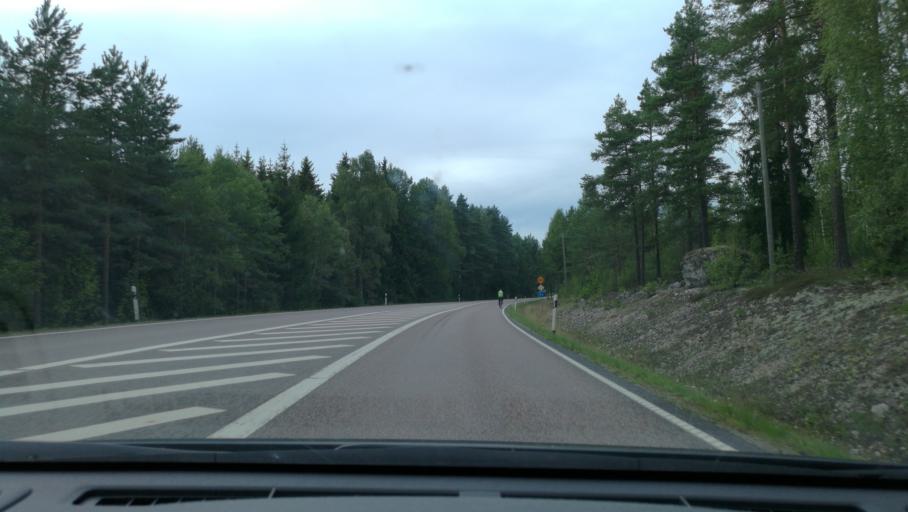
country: SE
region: Vaestmanland
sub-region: Kungsors Kommun
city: Kungsoer
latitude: 59.2885
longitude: 16.1108
